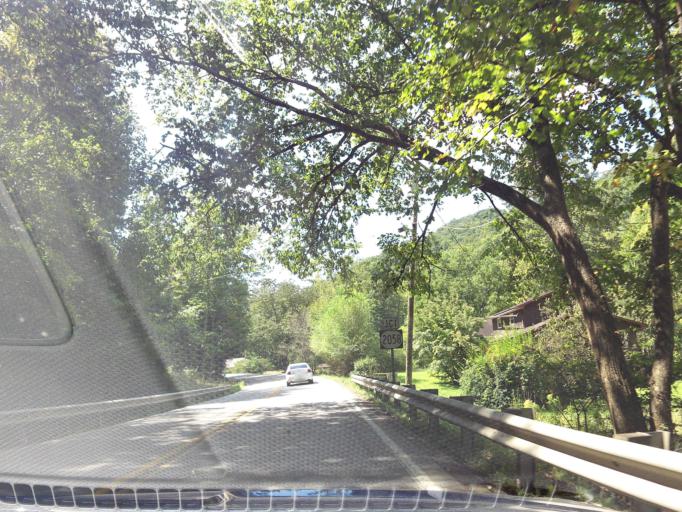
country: US
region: Kentucky
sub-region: Harlan County
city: Loyall
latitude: 36.9591
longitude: -83.3948
